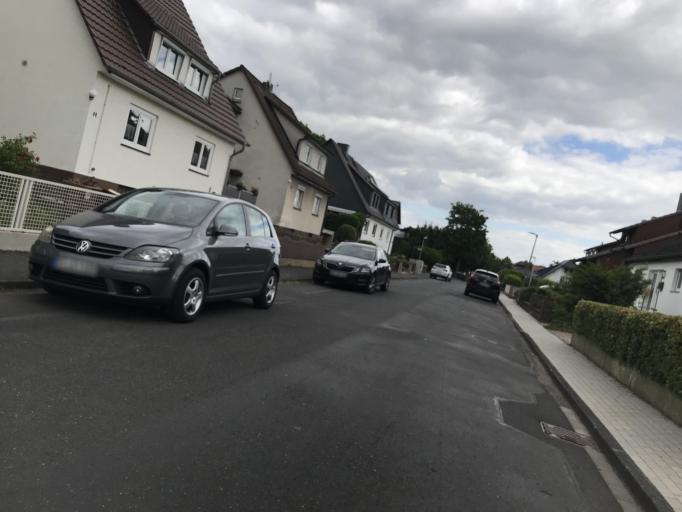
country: DE
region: Hesse
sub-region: Regierungsbezirk Kassel
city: Baunatal
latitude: 51.2508
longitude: 9.3927
